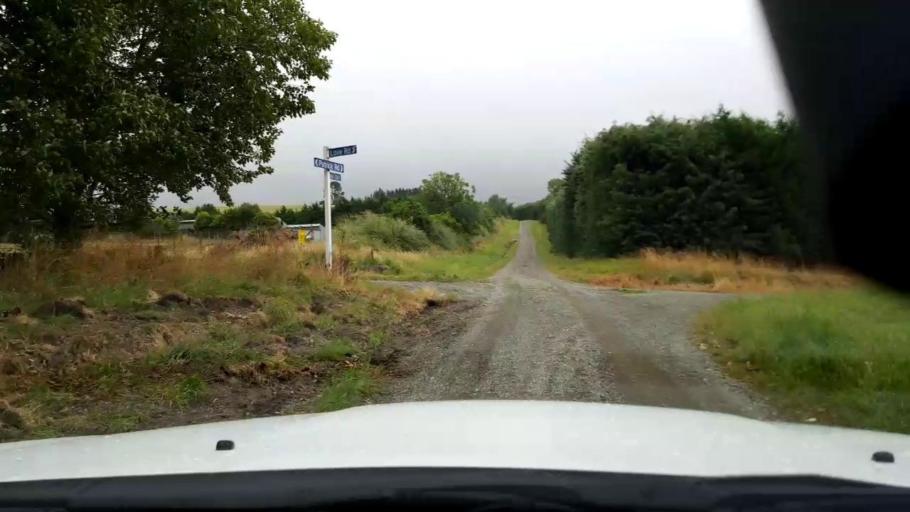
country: NZ
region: Canterbury
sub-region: Timaru District
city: Pleasant Point
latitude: -44.1024
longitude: 171.1334
